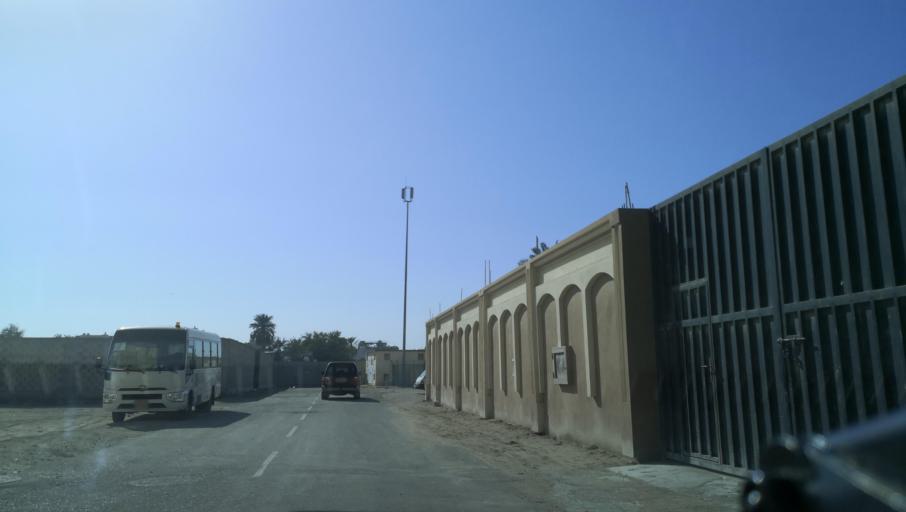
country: BH
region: Muharraq
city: Al Hadd
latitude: 26.2556
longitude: 50.6357
